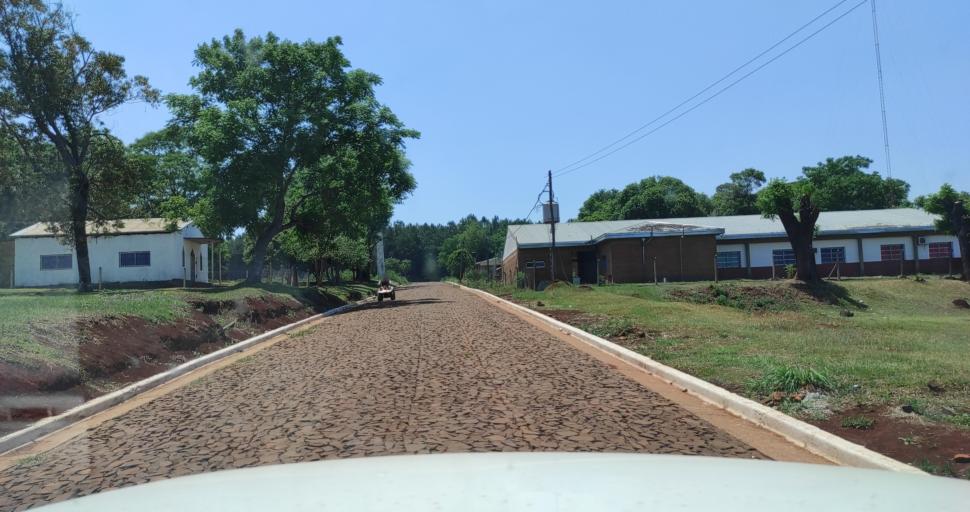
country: AR
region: Misiones
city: Santo Pipo
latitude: -27.1087
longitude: -55.3443
